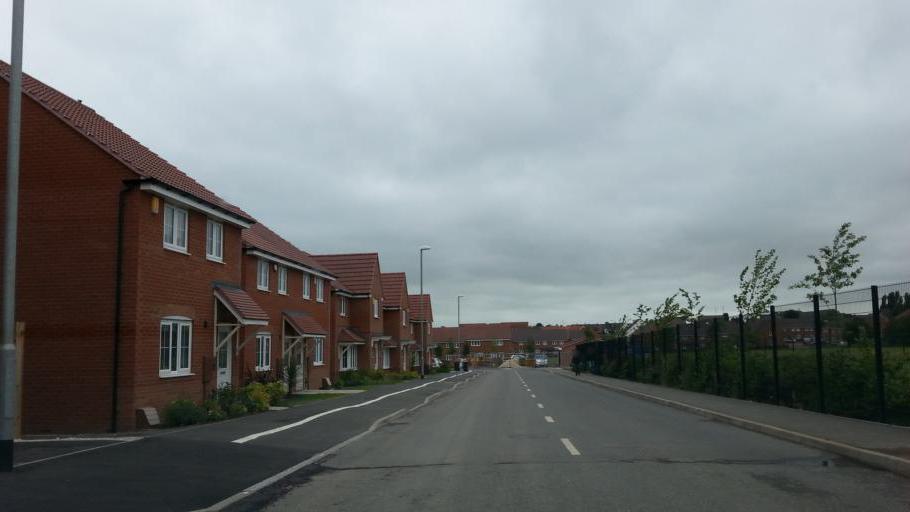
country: GB
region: England
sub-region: Nottinghamshire
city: Hucknall
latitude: 53.0410
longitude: -1.1920
